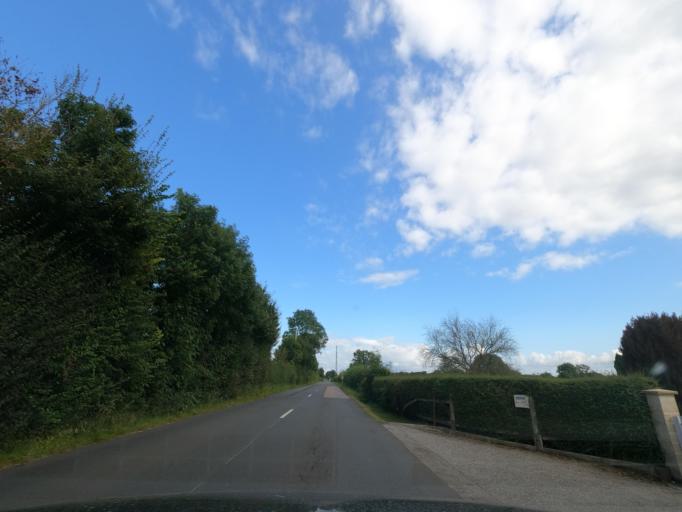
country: FR
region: Lower Normandy
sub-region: Departement de l'Orne
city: Gace
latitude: 48.7589
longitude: 0.1867
